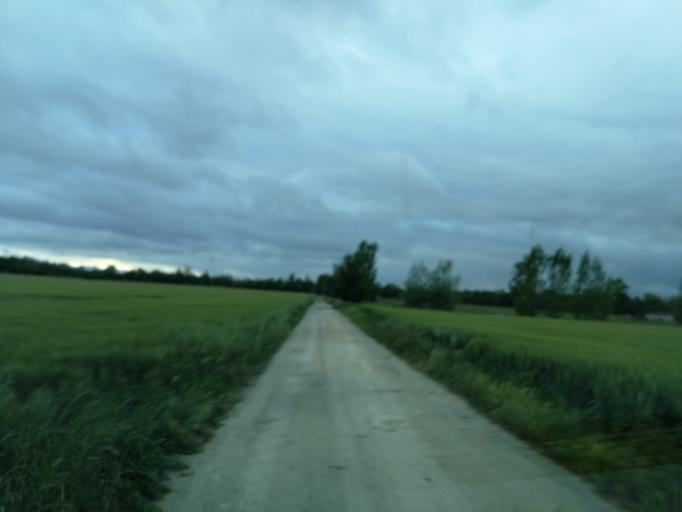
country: FR
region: Poitou-Charentes
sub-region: Departement de la Charente-Maritime
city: Marans
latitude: 46.3577
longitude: -0.9473
